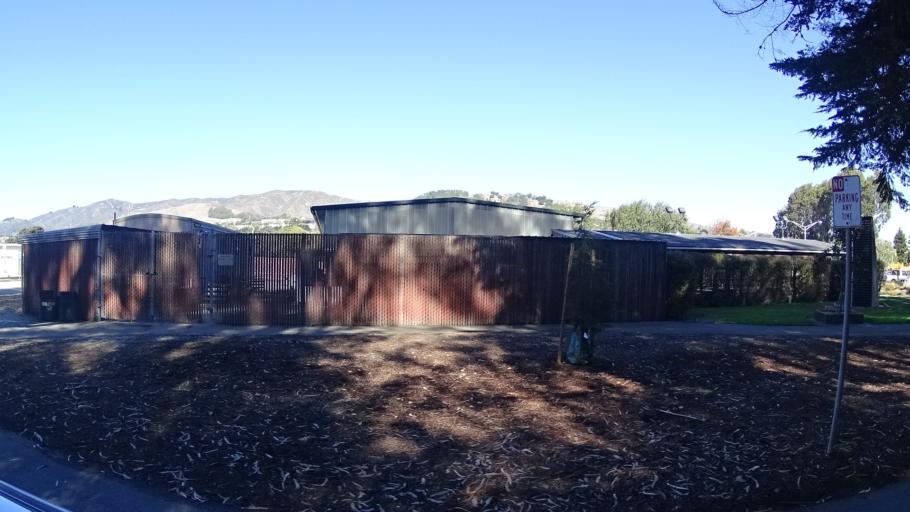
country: US
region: California
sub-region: San Mateo County
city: South San Francisco
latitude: 37.6544
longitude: -122.4279
